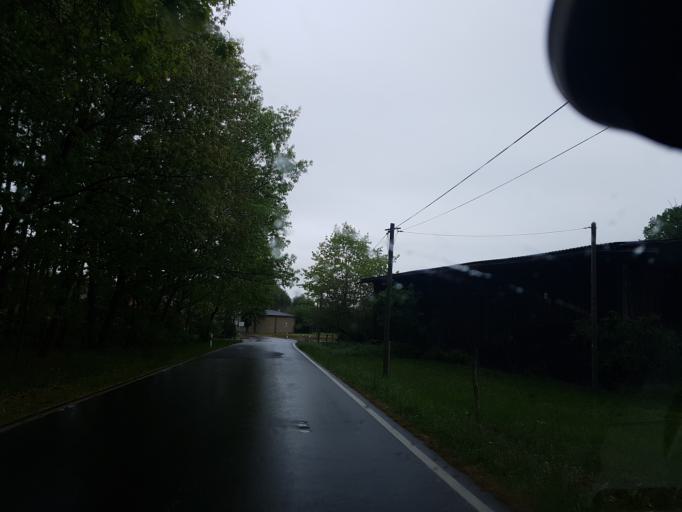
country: DE
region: Saxony
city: Gross Duben
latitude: 51.6645
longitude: 14.4719
